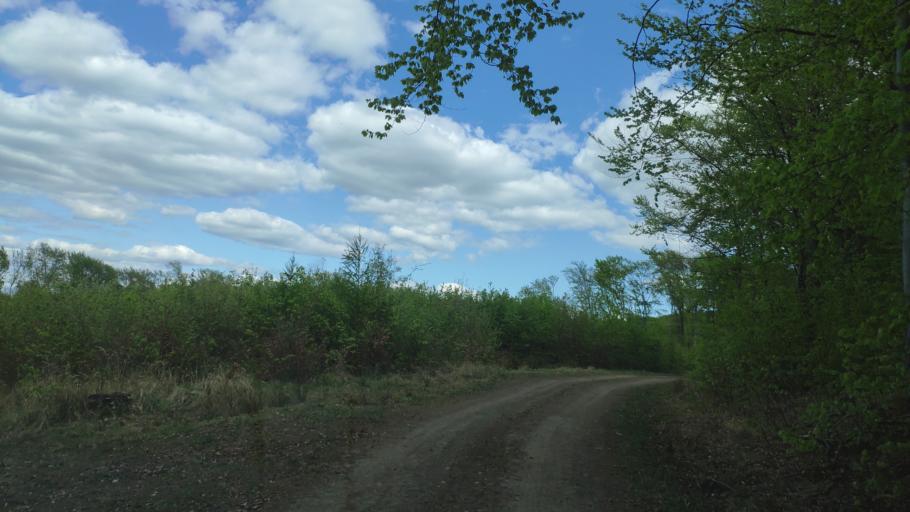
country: SK
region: Kosicky
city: Kosice
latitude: 48.6610
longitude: 21.4497
